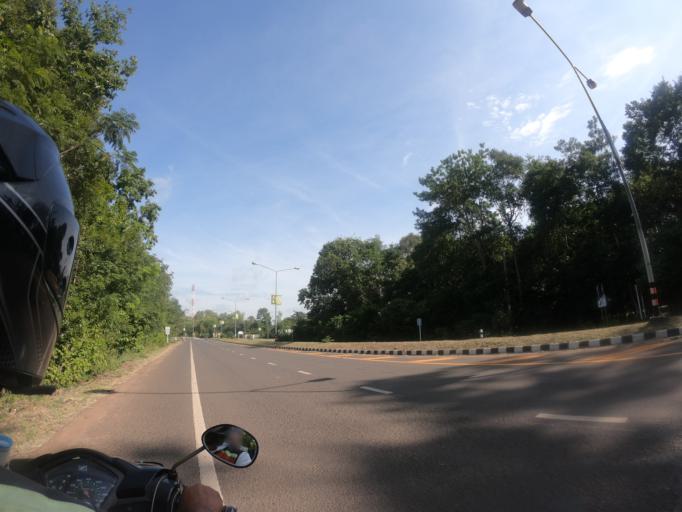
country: TH
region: Surin
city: Kap Choeng
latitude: 14.4502
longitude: 103.6994
